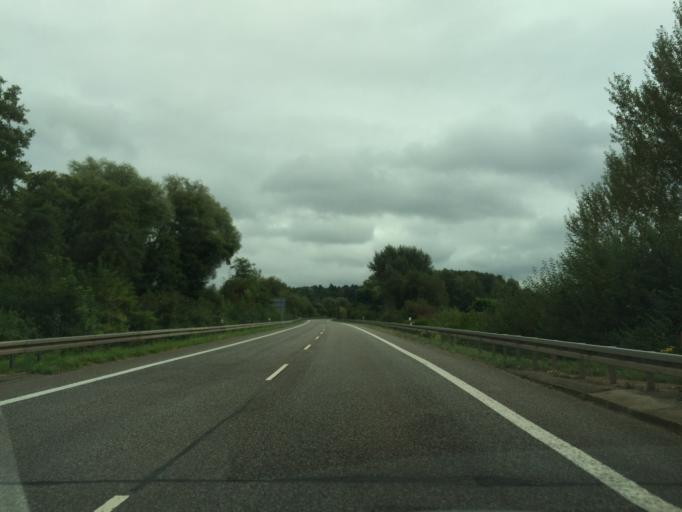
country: DE
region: Saarland
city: Beckingen
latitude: 49.3846
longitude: 6.6932
